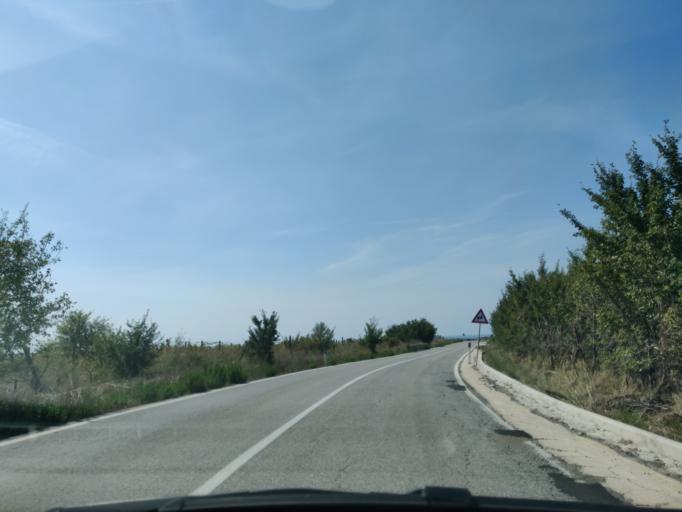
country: IT
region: Latium
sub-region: Provincia di Viterbo
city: Tarquinia
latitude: 42.2254
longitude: 11.7952
